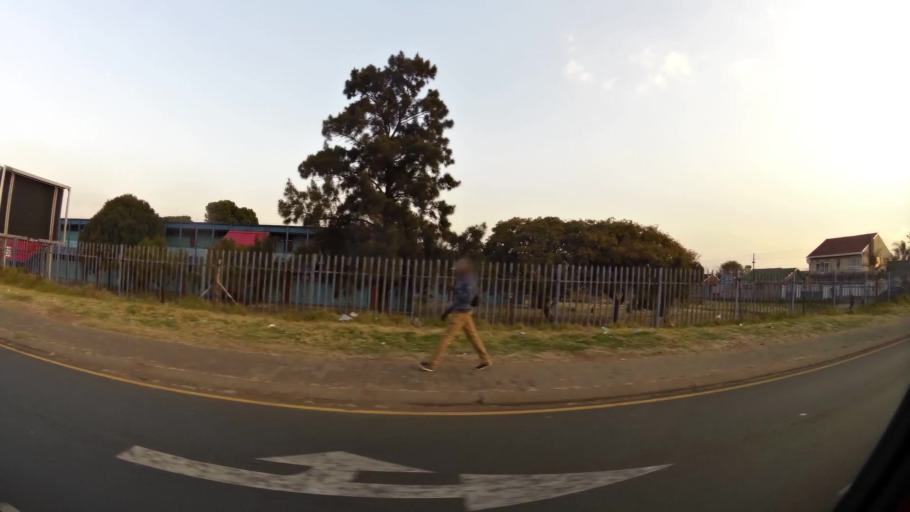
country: ZA
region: Gauteng
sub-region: City of Johannesburg Metropolitan Municipality
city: Soweto
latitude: -26.2920
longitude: 27.9007
